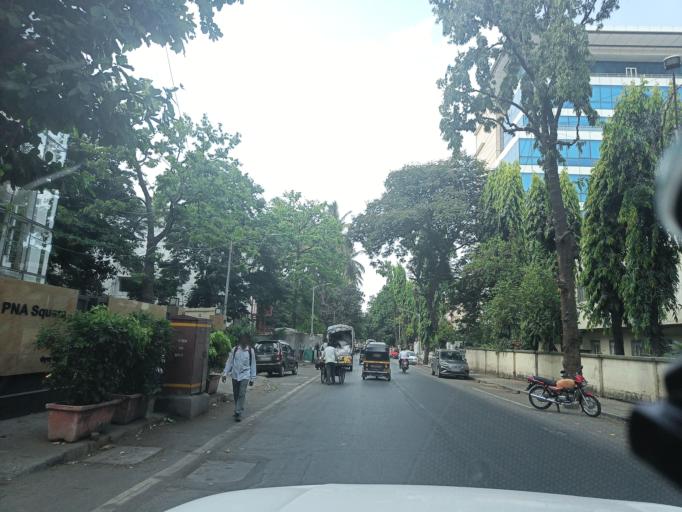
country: IN
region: Maharashtra
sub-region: Mumbai Suburban
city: Powai
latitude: 19.1174
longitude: 72.8684
